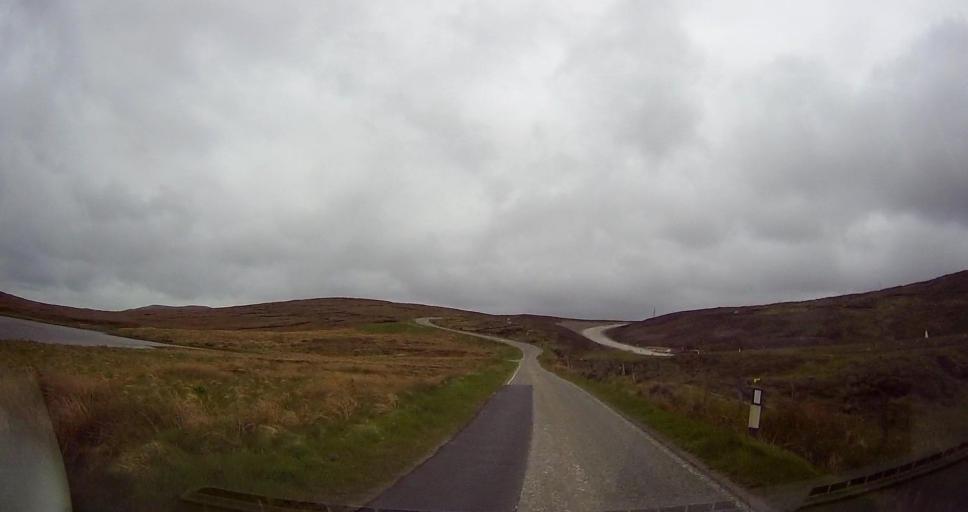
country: GB
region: Scotland
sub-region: Shetland Islands
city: Lerwick
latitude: 60.2788
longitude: -1.2541
